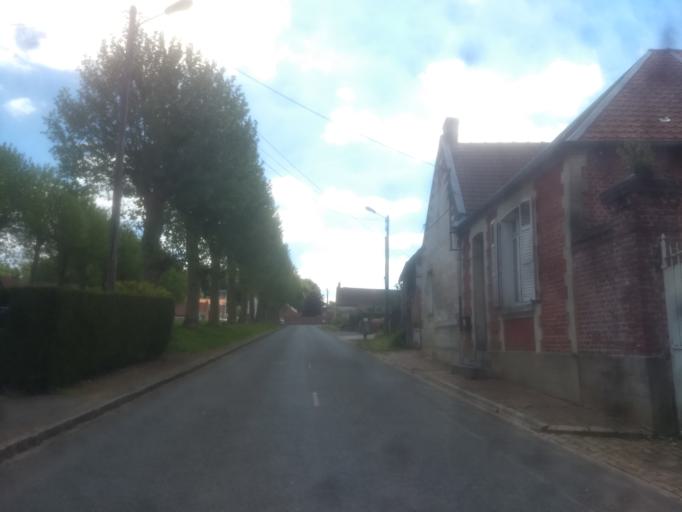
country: FR
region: Nord-Pas-de-Calais
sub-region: Departement du Pas-de-Calais
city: Riviere
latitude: 50.2301
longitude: 2.6785
